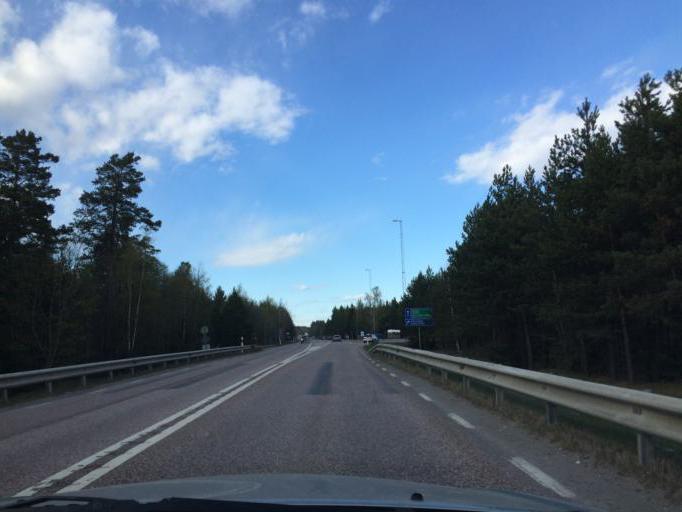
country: SE
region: Vaestmanland
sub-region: Hallstahammars Kommun
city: Kolback
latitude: 59.5650
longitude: 16.3483
